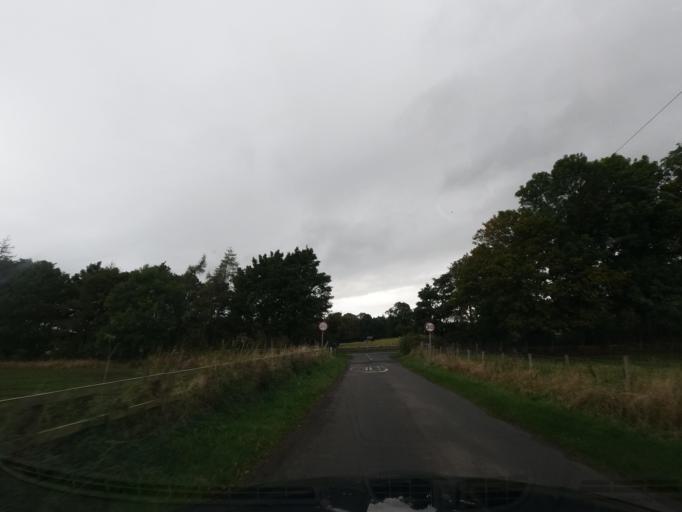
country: GB
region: England
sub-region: Northumberland
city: Ford
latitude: 55.6287
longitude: -2.0893
